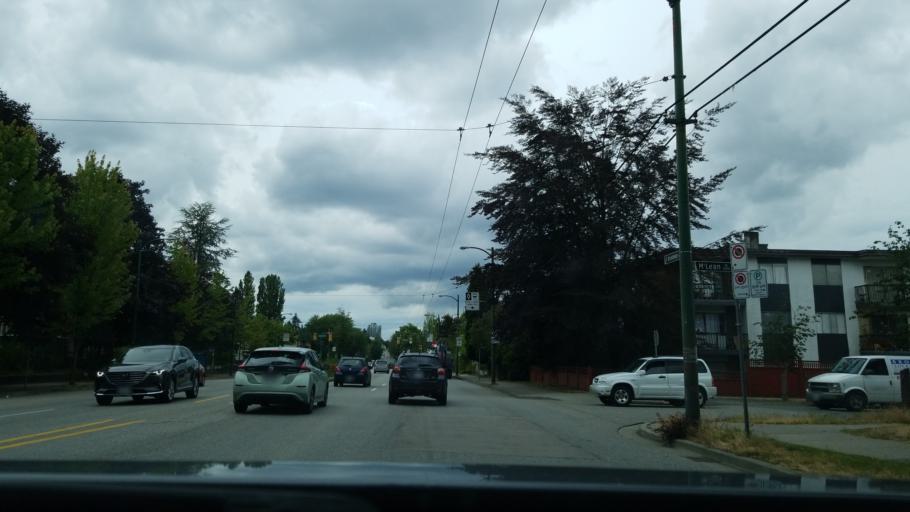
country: CA
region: British Columbia
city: Vancouver
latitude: 49.2624
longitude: -123.0753
